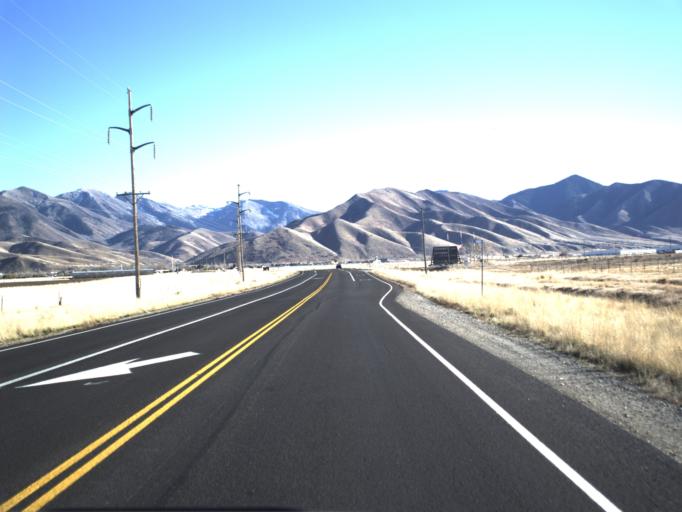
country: US
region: Utah
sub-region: Tooele County
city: Tooele
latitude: 40.5449
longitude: -112.3392
